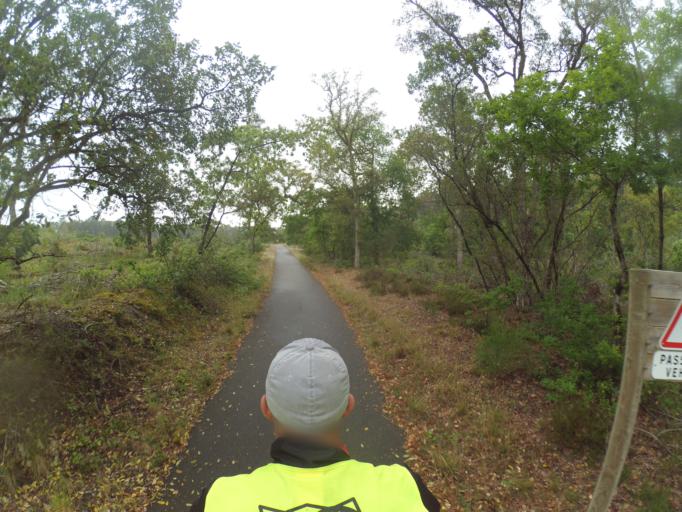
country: FR
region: Aquitaine
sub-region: Departement des Landes
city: Mimizan
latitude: 44.2198
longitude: -1.2408
